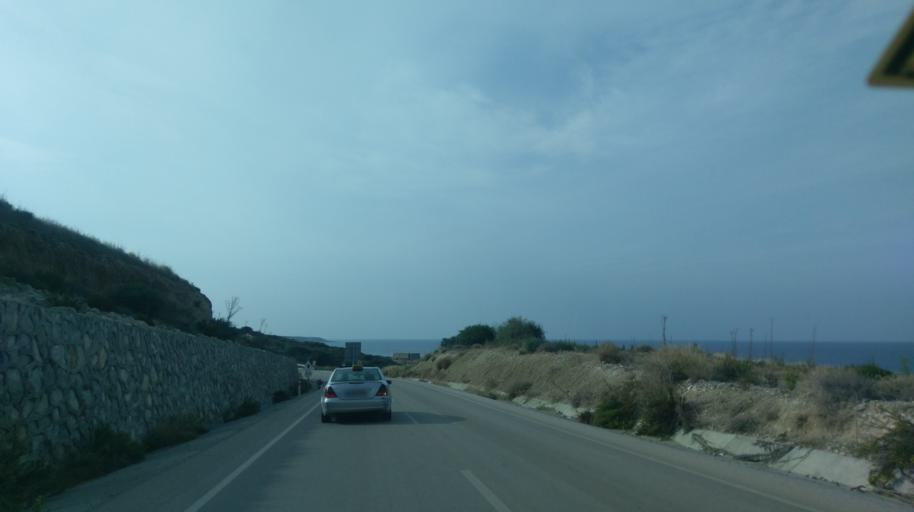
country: CY
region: Ammochostos
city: Trikomo
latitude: 35.4119
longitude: 33.8445
